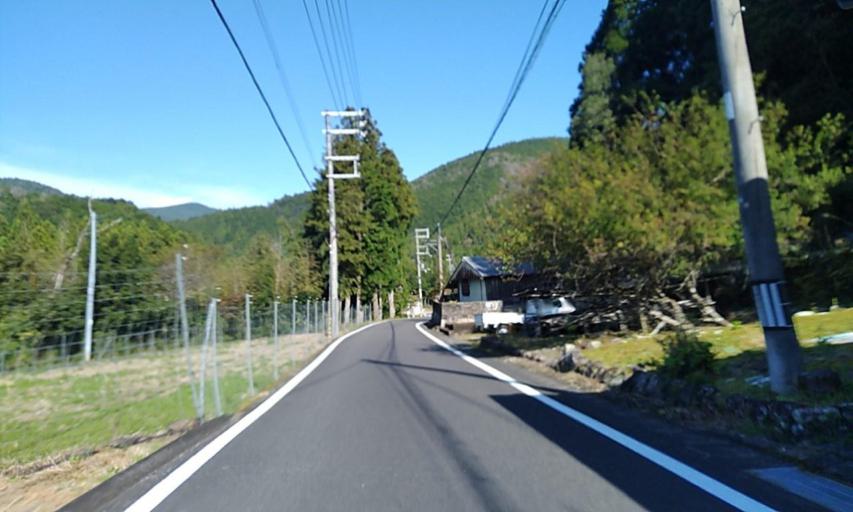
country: JP
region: Wakayama
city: Shingu
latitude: 33.9287
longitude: 135.9795
